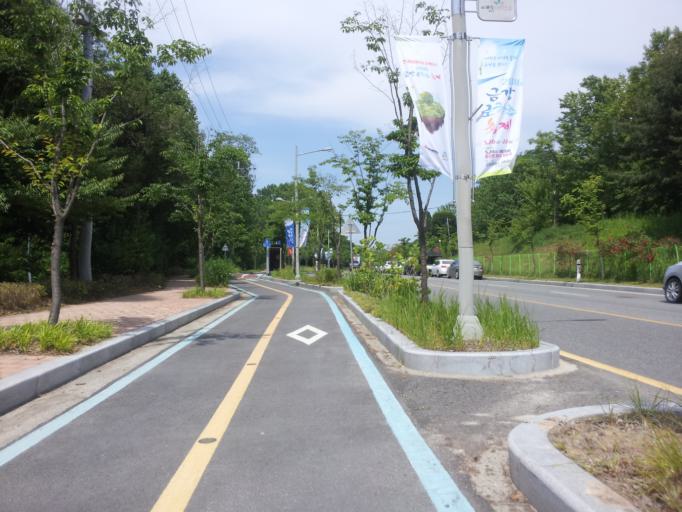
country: KR
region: Daejeon
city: Sintansin
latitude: 36.4704
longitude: 127.4724
